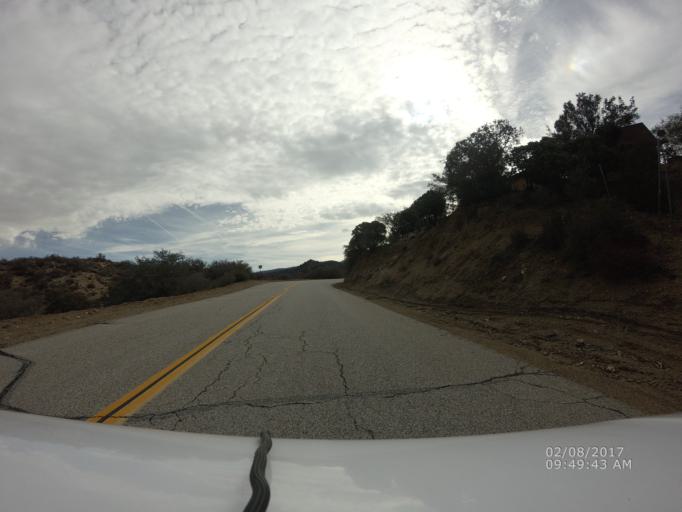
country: US
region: California
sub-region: San Bernardino County
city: Pinon Hills
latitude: 34.4298
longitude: -117.8103
